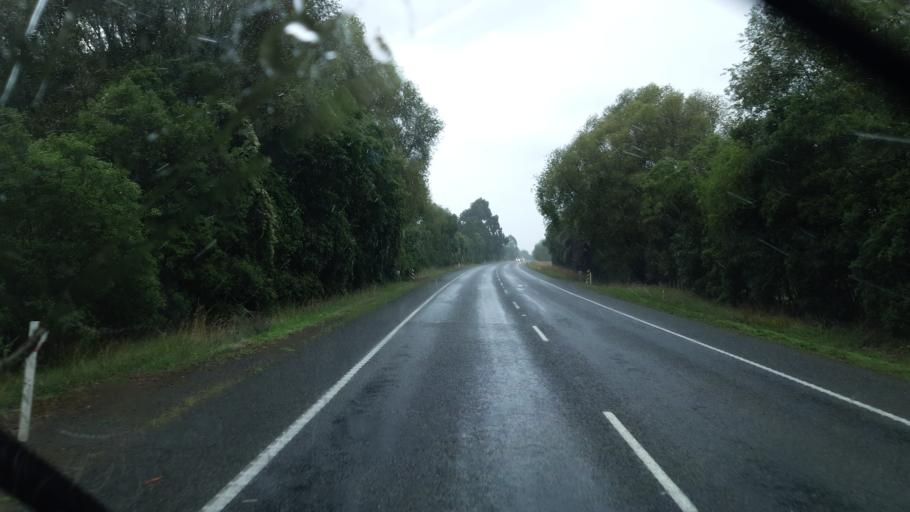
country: NZ
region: Tasman
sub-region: Tasman District
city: Brightwater
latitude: -41.3815
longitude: 173.0866
